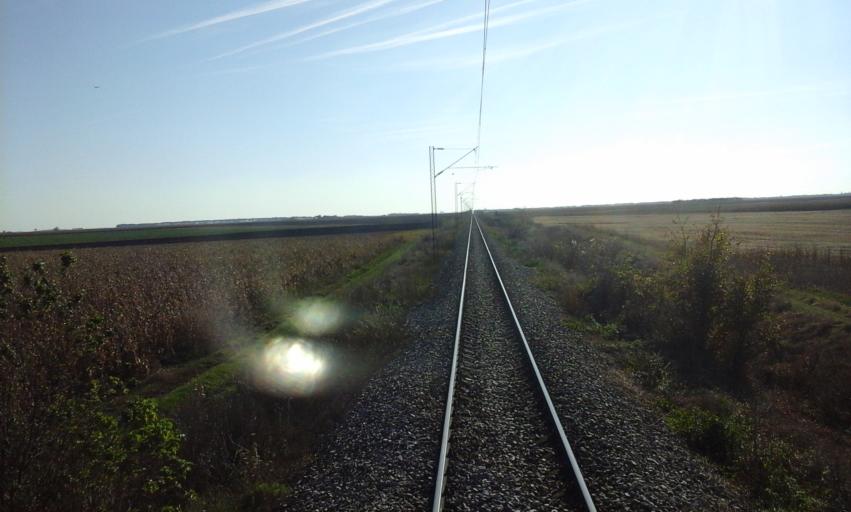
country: RS
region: Autonomna Pokrajina Vojvodina
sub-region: Severnobacki Okrug
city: Backa Topola
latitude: 45.9138
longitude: 19.6643
